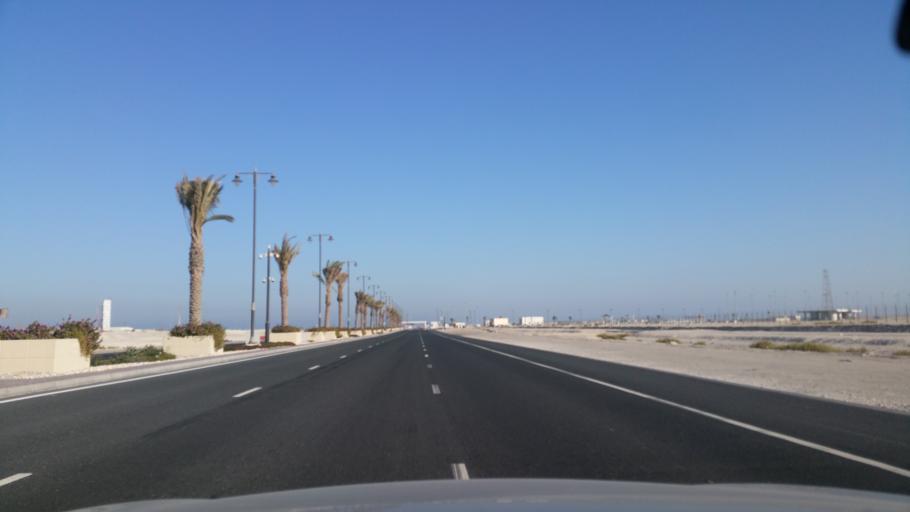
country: QA
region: Al Wakrah
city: Umm Sa'id
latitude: 25.0566
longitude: 51.5972
